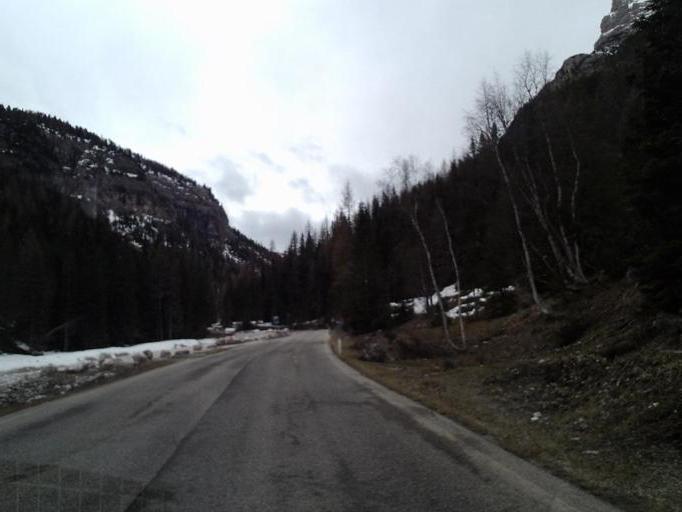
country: IT
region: Veneto
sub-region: Provincia di Belluno
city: Cortina d'Ampezzo
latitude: 46.5998
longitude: 12.2413
